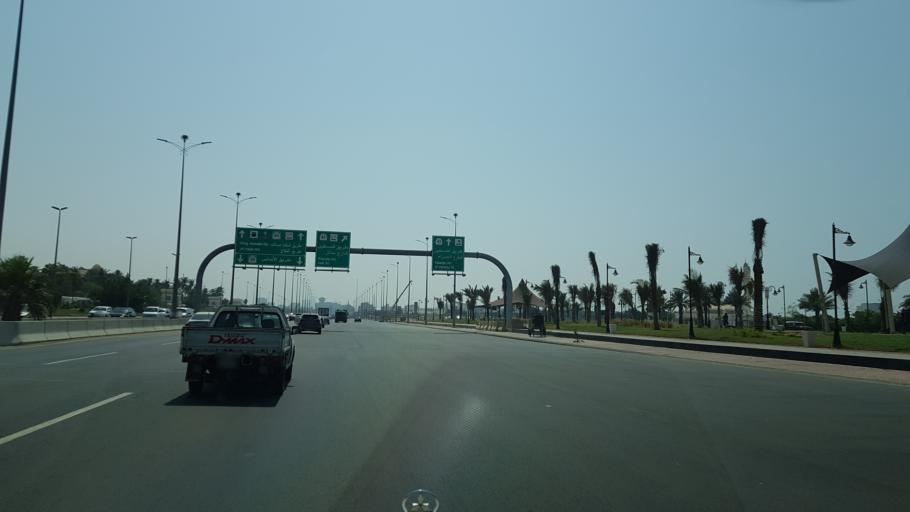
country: SA
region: Makkah
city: Jeddah
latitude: 21.5352
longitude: 39.1582
